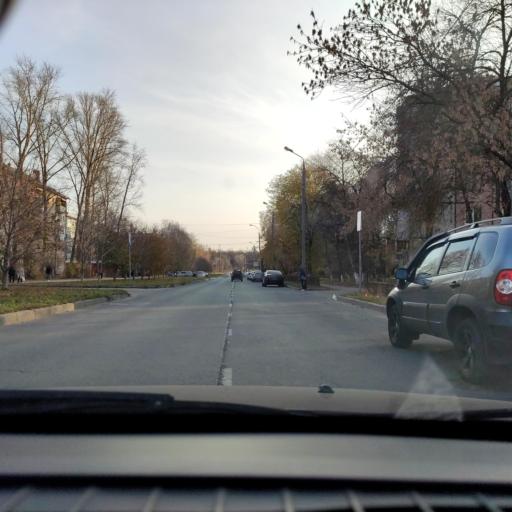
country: RU
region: Samara
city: Tol'yatti
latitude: 53.5022
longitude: 49.4008
